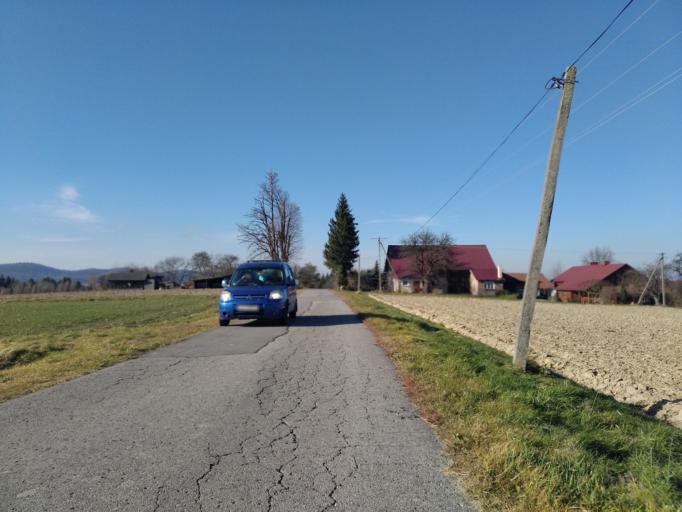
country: PL
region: Subcarpathian Voivodeship
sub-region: Powiat strzyzowski
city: Wysoka Strzyzowska
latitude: 49.8168
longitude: 21.7723
